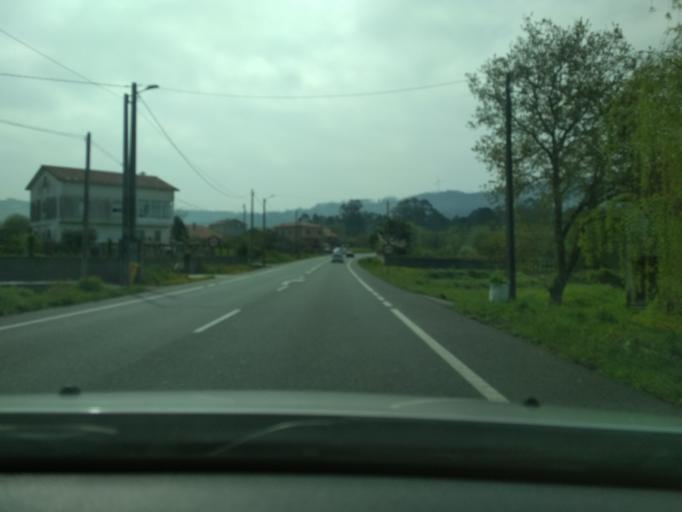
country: ES
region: Galicia
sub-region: Provincia de Pontevedra
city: Catoira
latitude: 42.6696
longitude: -8.7062
